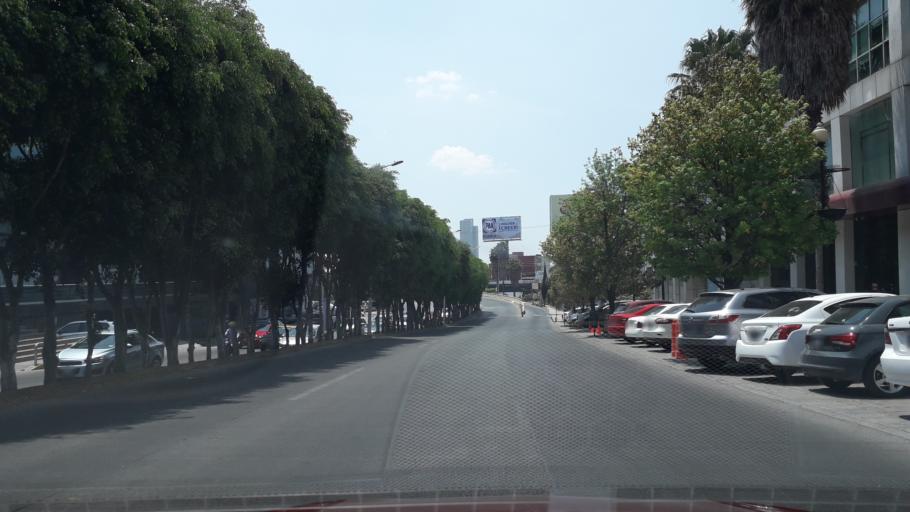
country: MX
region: Puebla
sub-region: San Pedro Cholula
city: Santiago Momoxpan
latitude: 19.0513
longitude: -98.2383
